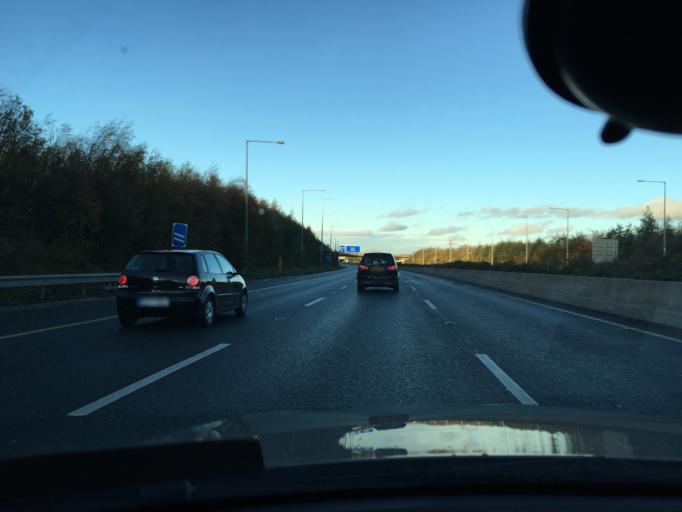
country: IE
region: Leinster
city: Kinsealy-Drinan
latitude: 53.4365
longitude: -6.2103
